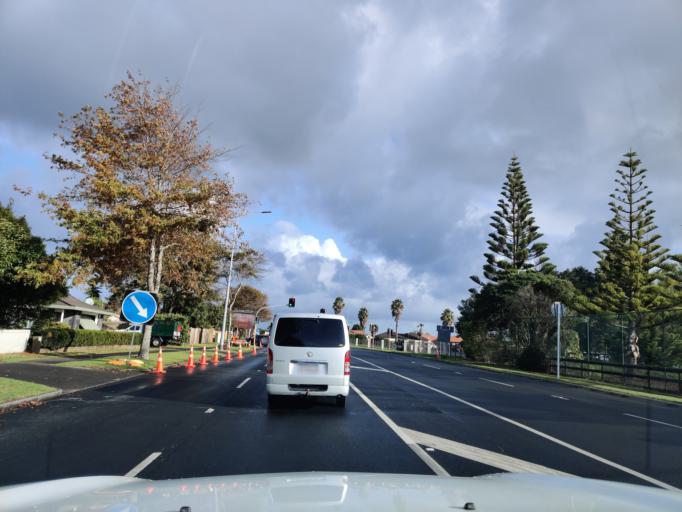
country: NZ
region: Auckland
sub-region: Auckland
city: Pakuranga
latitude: -36.9189
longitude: 174.9132
